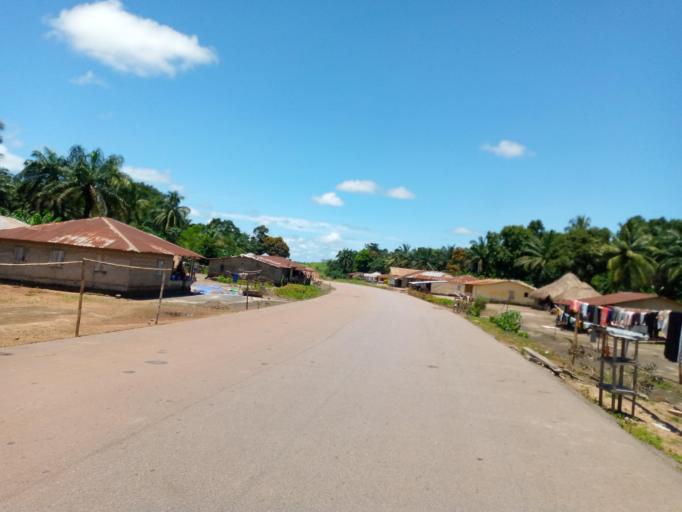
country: SL
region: Northern Province
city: Makeni
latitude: 9.0682
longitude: -12.1767
